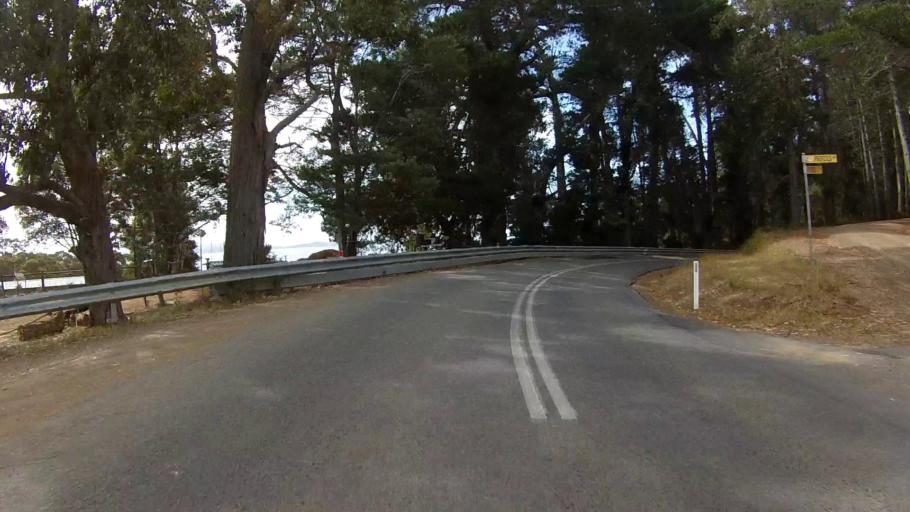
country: AU
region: Tasmania
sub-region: Kingborough
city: Kettering
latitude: -43.2000
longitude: 147.2521
